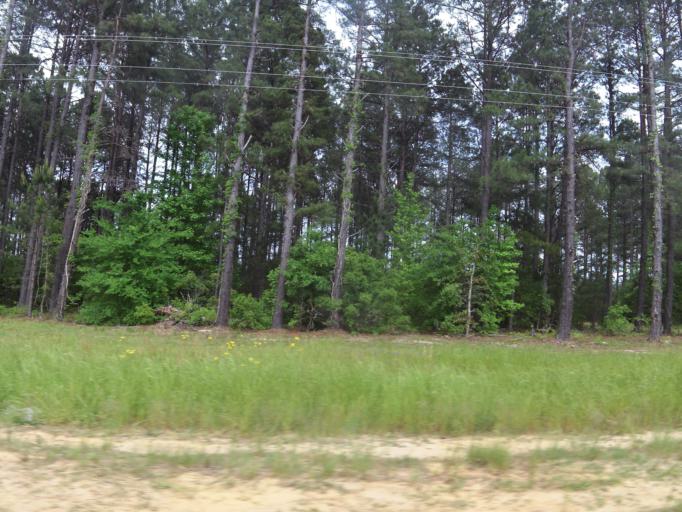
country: US
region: Georgia
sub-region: McDuffie County
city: Thomson
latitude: 33.3458
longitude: -82.4596
